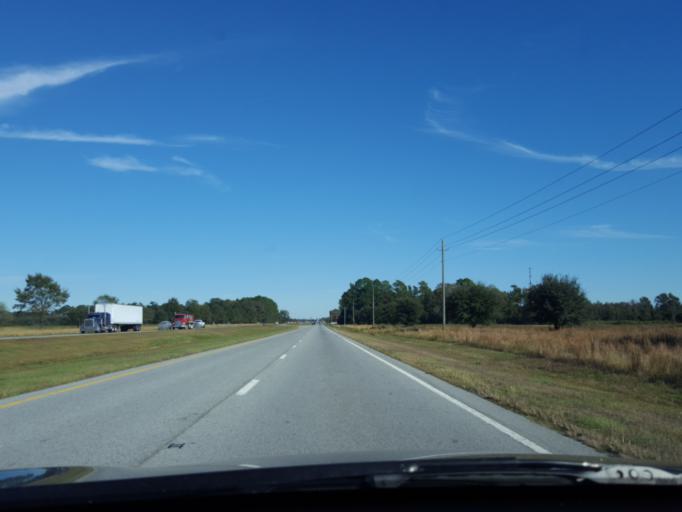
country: US
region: North Carolina
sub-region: Pitt County
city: Greenville
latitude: 35.6256
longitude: -77.2895
